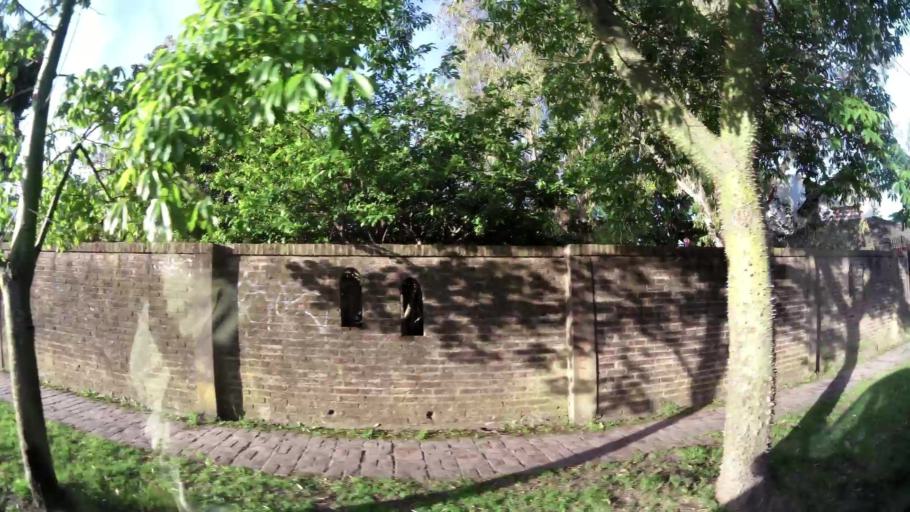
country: AR
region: Buenos Aires
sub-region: Partido de Almirante Brown
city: Adrogue
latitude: -34.7974
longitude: -58.3551
